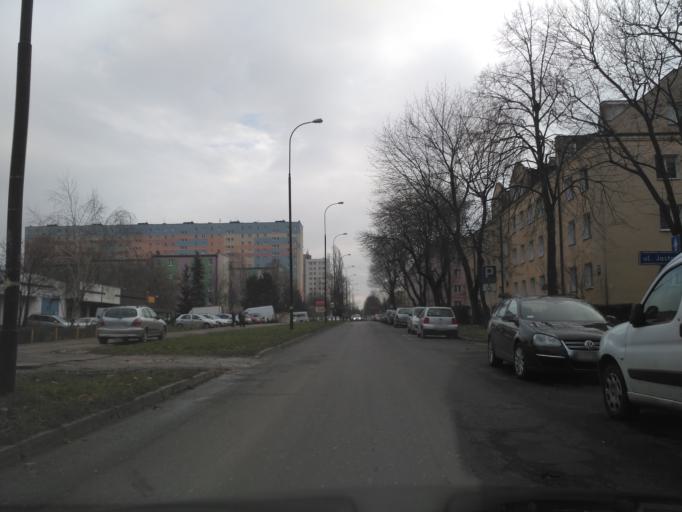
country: PL
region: Lublin Voivodeship
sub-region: Powiat lubelski
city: Lublin
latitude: 51.2355
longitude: 22.5898
